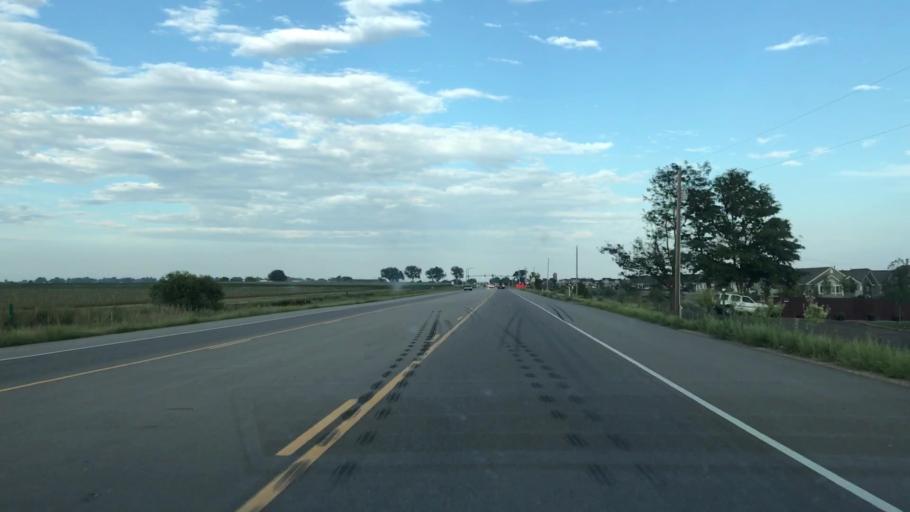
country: US
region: Colorado
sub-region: Boulder County
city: Longmont
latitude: 40.2032
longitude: -105.0797
